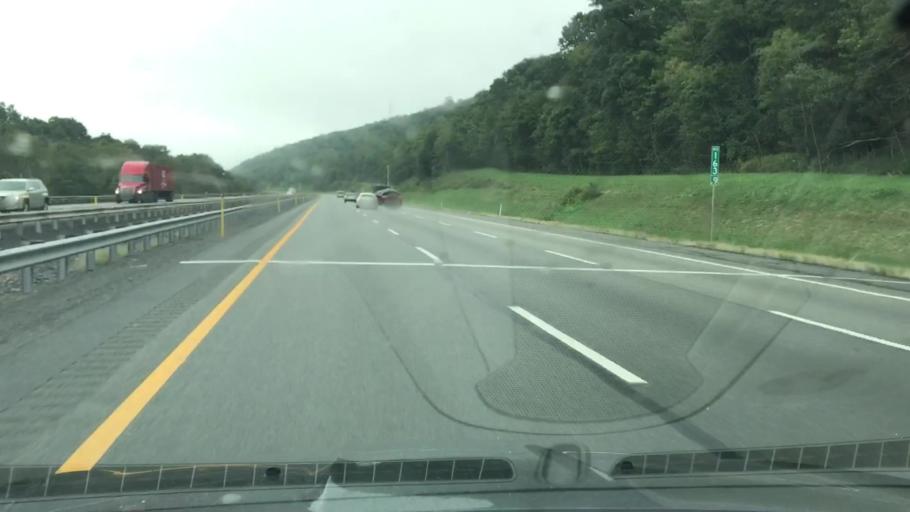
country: US
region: Pennsylvania
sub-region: Bedford County
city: Earlston
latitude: 40.0005
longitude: -78.2183
